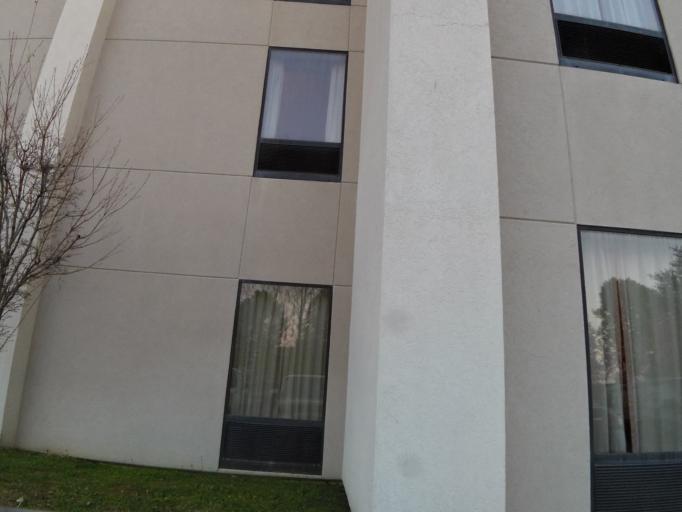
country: US
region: Tennessee
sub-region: Robertson County
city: Springfield
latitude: 36.4883
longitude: -86.8785
